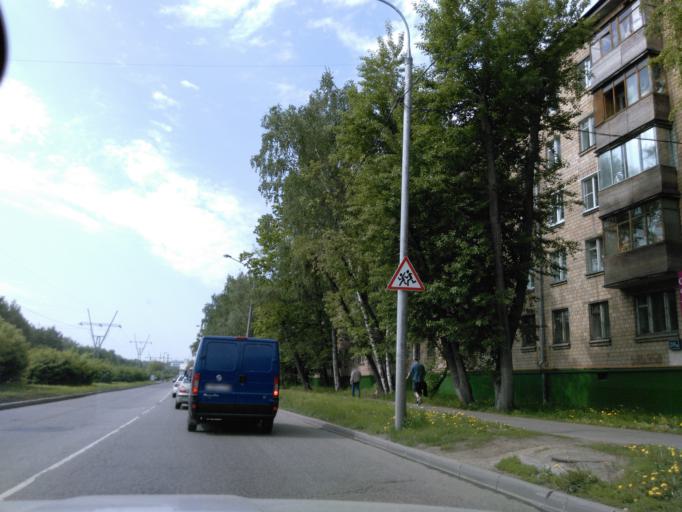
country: RU
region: Moscow
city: Golovinskiy
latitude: 55.8504
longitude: 37.5086
